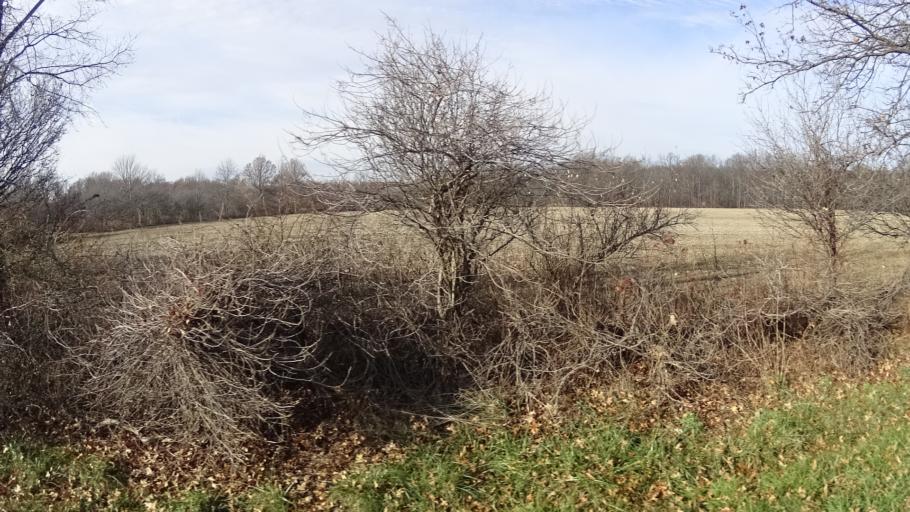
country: US
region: Ohio
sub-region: Lorain County
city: Grafton
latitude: 41.2117
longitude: -82.0433
